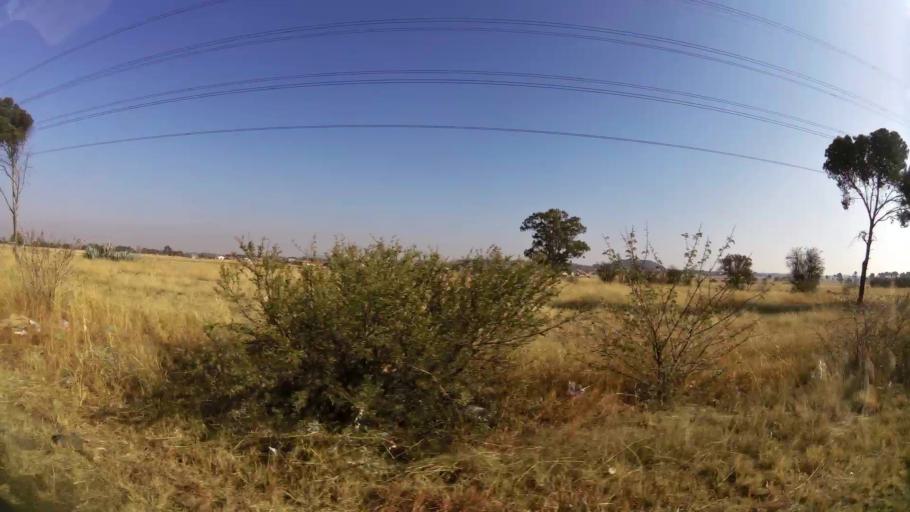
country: ZA
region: Orange Free State
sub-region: Mangaung Metropolitan Municipality
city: Bloemfontein
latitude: -29.1844
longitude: 26.1871
